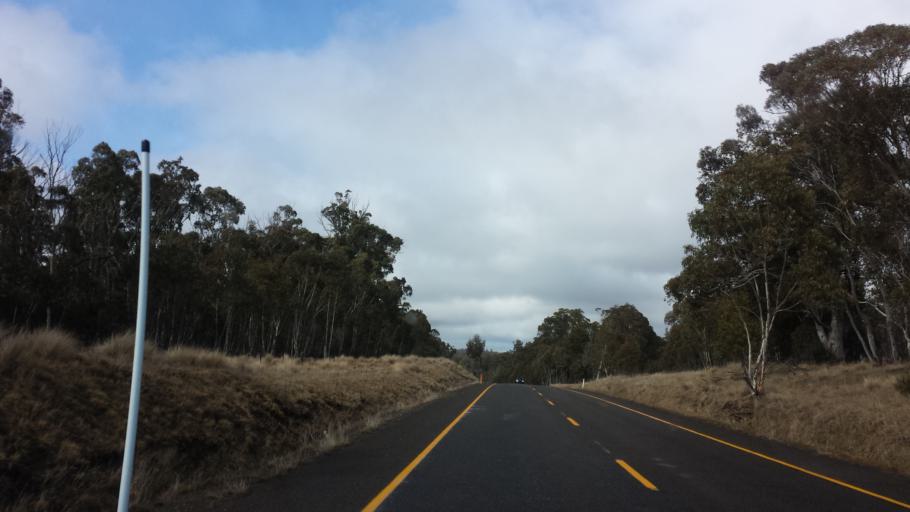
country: AU
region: Victoria
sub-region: Alpine
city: Mount Beauty
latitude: -37.0636
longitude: 147.3370
